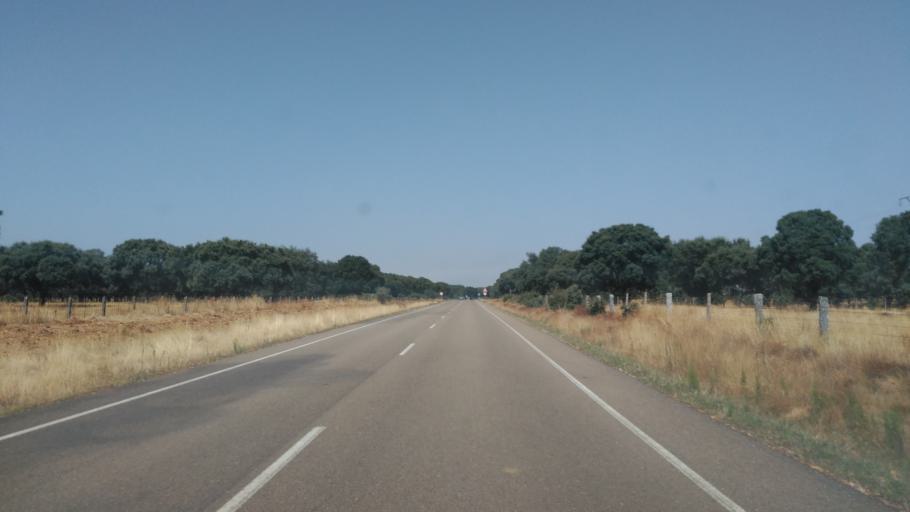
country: ES
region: Castille and Leon
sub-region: Provincia de Salamanca
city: Abusejo
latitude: 40.6805
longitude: -6.1290
